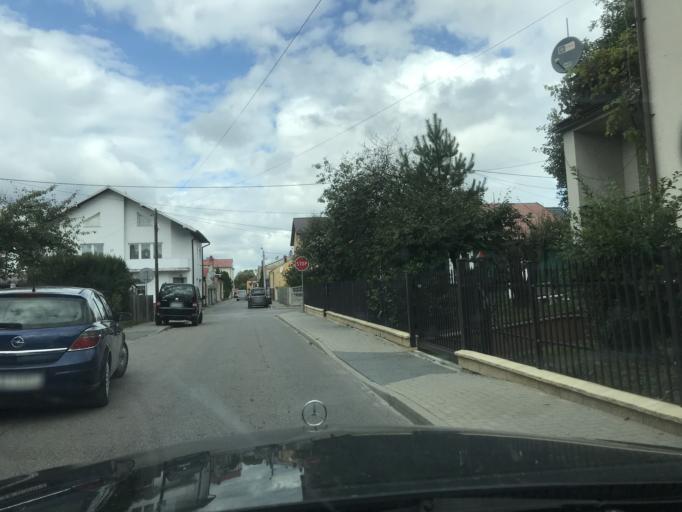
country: PL
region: Lublin Voivodeship
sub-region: Powiat janowski
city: Janow Lubelski
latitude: 50.7065
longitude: 22.4134
